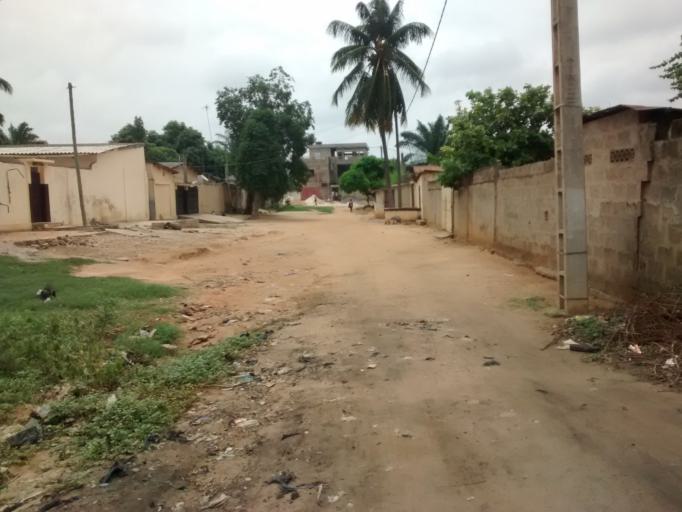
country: TG
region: Maritime
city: Lome
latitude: 6.1753
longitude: 1.1842
